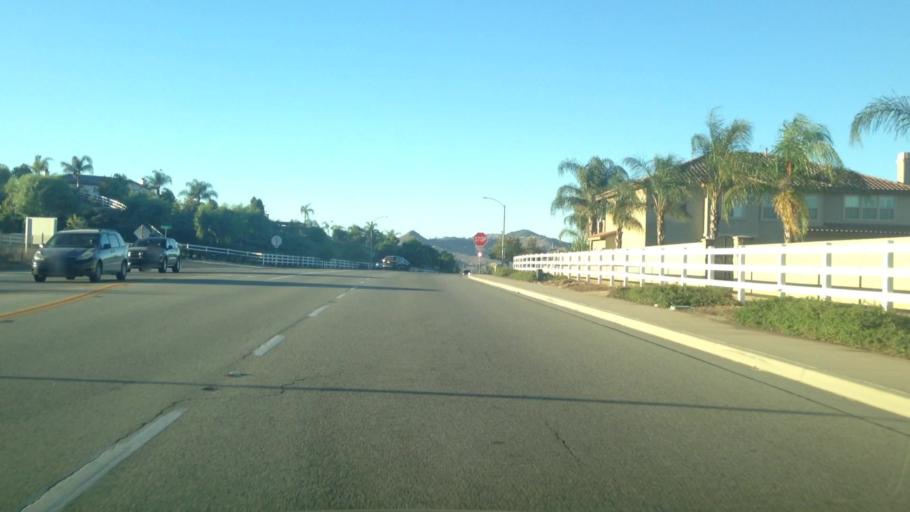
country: US
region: California
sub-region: Riverside County
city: Woodcrest
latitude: 33.8662
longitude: -117.3663
